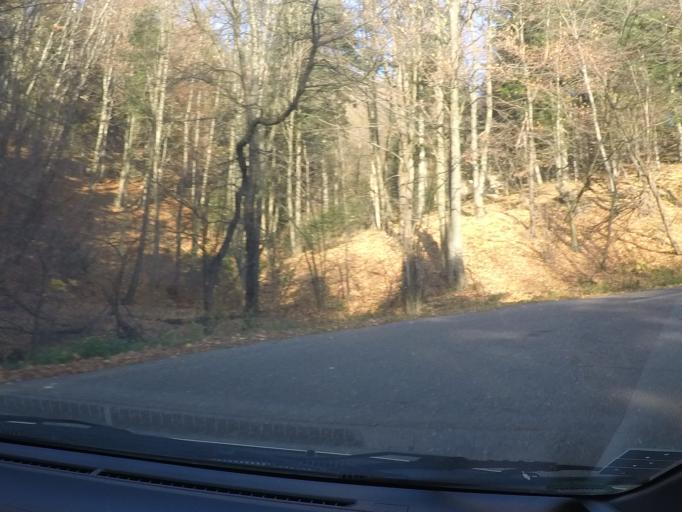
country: SK
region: Banskobystricky
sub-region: Okres Banska Bystrica
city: Banska Stiavnica
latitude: 48.4698
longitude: 18.8606
